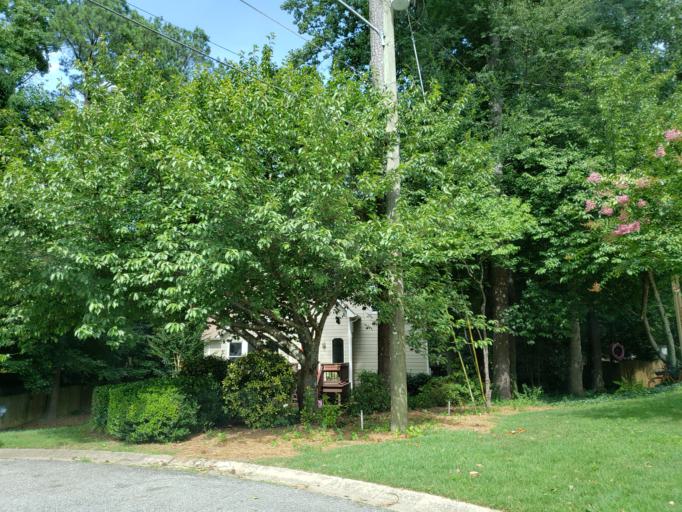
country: US
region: Georgia
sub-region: Cobb County
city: Smyrna
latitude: 33.8862
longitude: -84.5416
